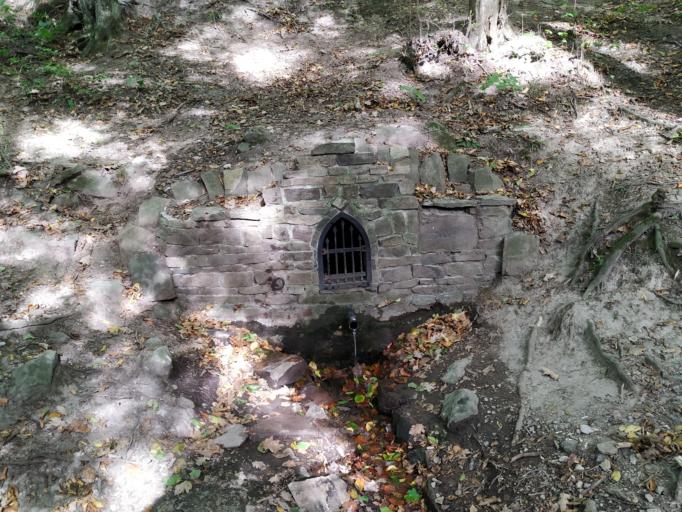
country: HU
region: Nograd
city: Diosjeno
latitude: 47.9794
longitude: 18.9938
